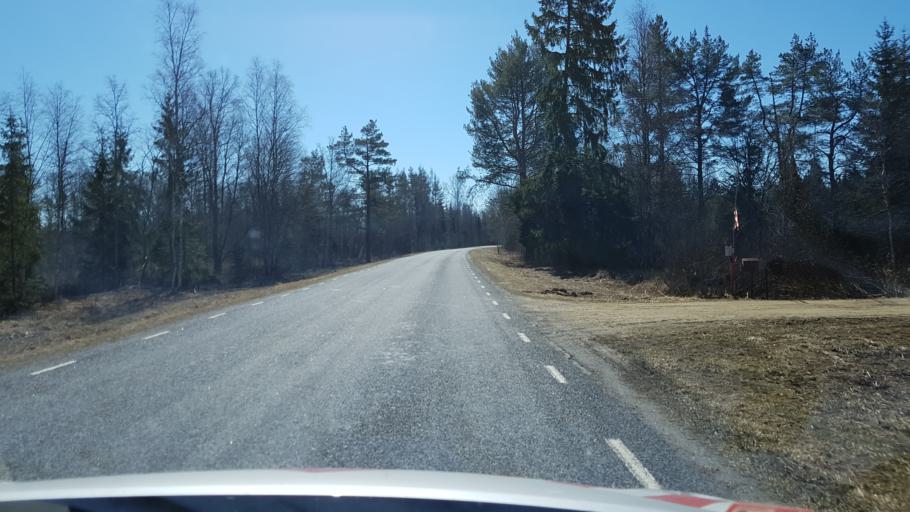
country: EE
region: Laeaene-Virumaa
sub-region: Haljala vald
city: Haljala
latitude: 59.4873
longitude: 26.2476
